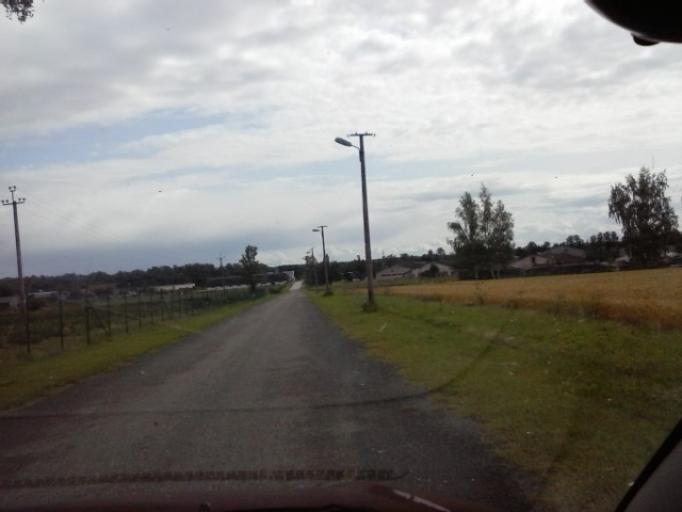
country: EE
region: Tartu
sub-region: Tartu linn
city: Tartu
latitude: 58.3631
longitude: 26.8750
